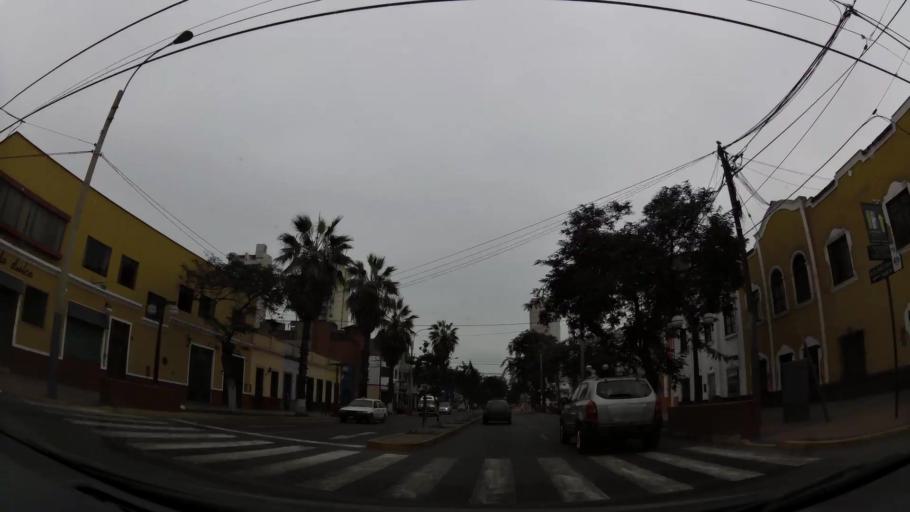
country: PE
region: Lima
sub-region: Lima
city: San Isidro
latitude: -12.0799
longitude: -77.0592
